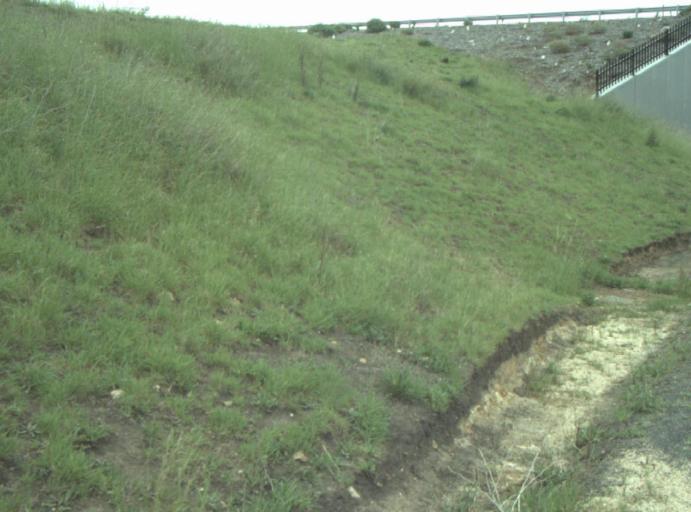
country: AU
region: Victoria
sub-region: Greater Geelong
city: Wandana Heights
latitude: -38.1843
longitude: 144.3031
